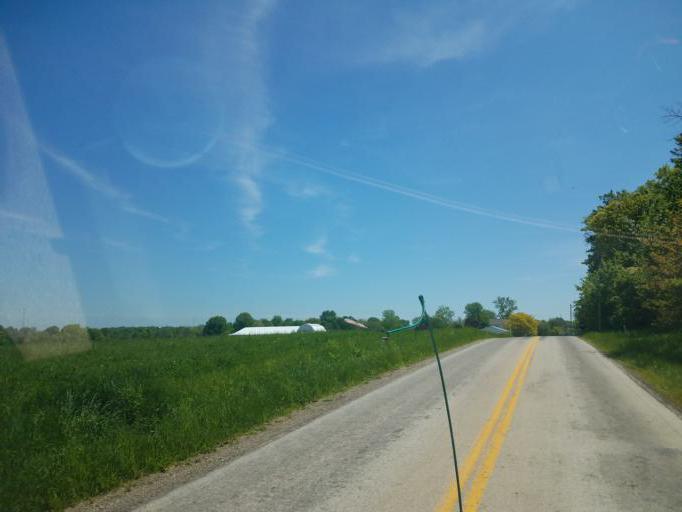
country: US
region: Ohio
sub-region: Ashland County
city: Ashland
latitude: 40.9450
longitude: -82.2295
